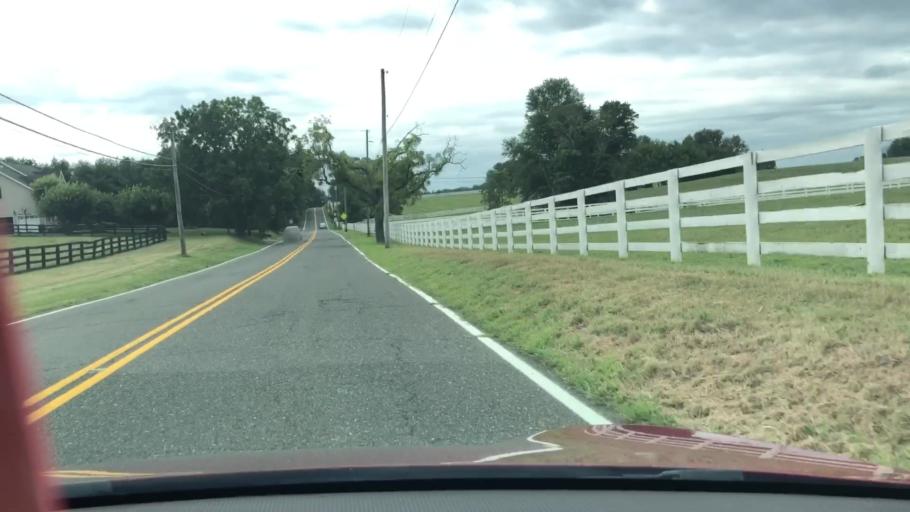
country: US
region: New Jersey
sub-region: Monmouth County
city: Shrewsbury
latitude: 40.1740
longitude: -74.5126
